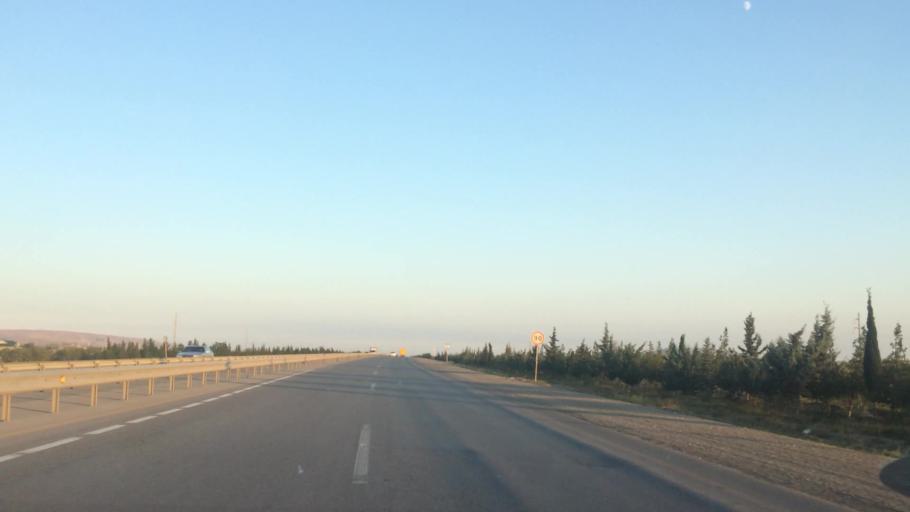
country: AZ
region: Haciqabul
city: Haciqabul
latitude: 40.0048
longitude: 49.1631
